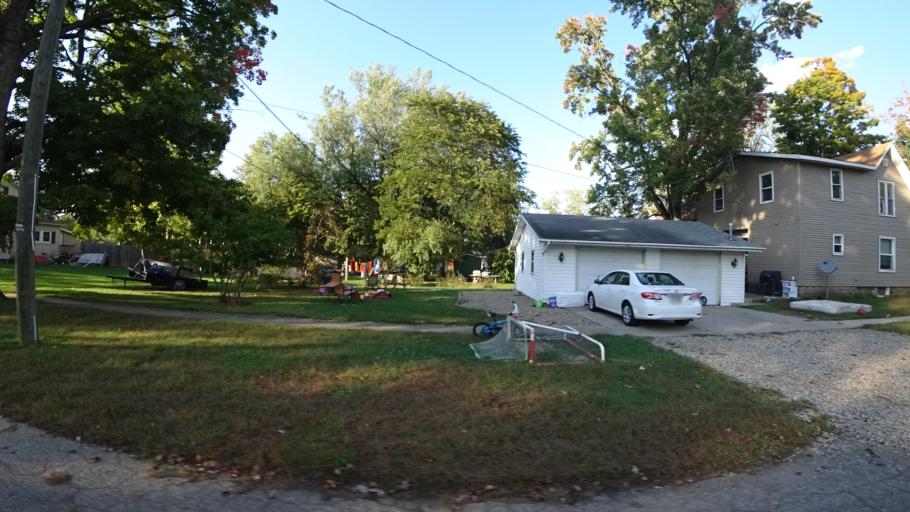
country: US
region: Michigan
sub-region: Saint Joseph County
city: Three Rivers
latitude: 41.9512
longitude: -85.6379
